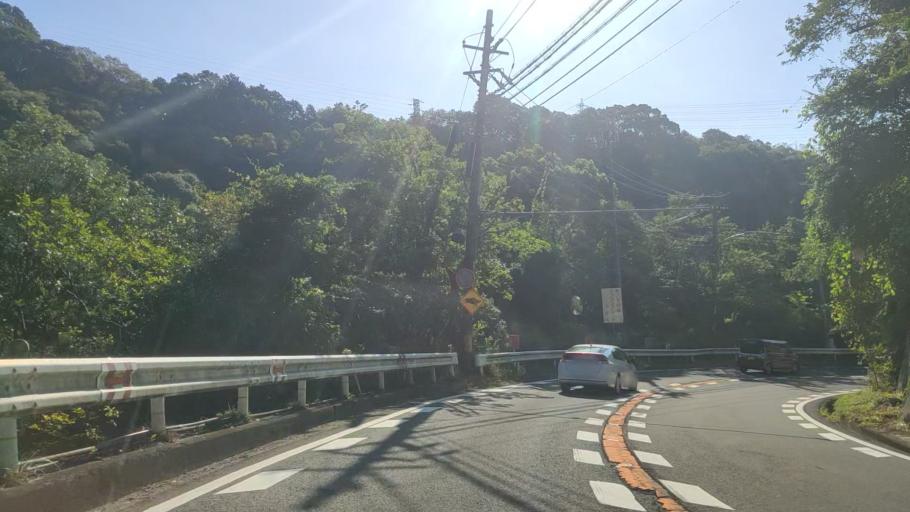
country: JP
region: Hyogo
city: Kobe
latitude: 34.7094
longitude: 135.1608
